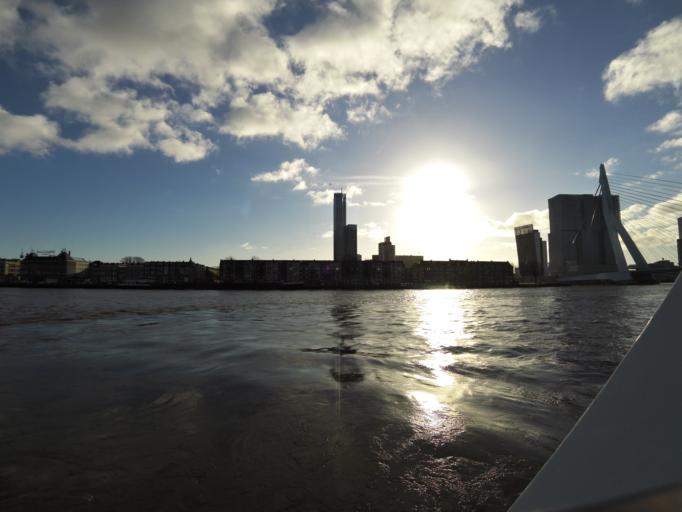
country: NL
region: South Holland
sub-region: Gemeente Rotterdam
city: Rotterdam
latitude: 51.9130
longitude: 4.4873
